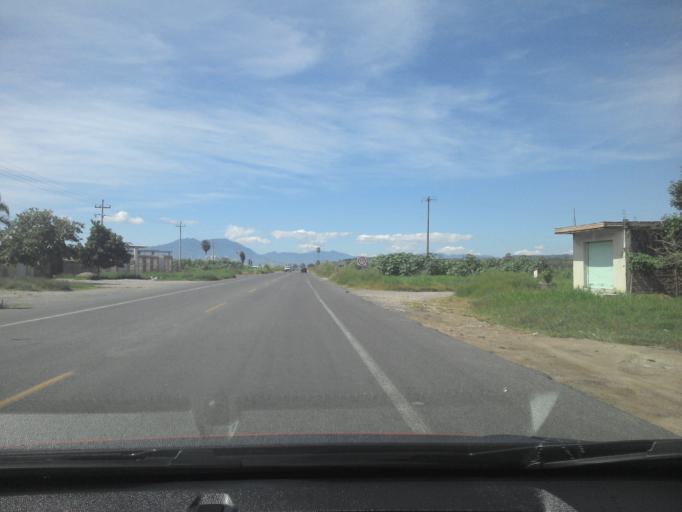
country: MX
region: Jalisco
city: El Refugio
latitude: 20.6667
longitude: -103.7421
